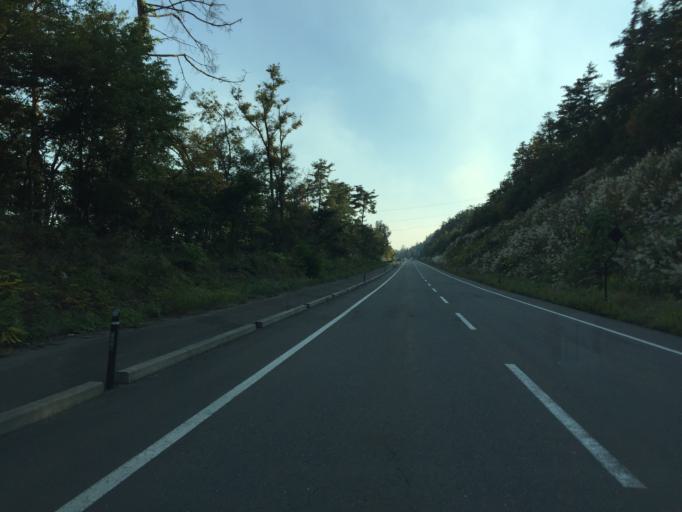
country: JP
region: Fukushima
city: Kitakata
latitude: 37.7143
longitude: 139.8686
